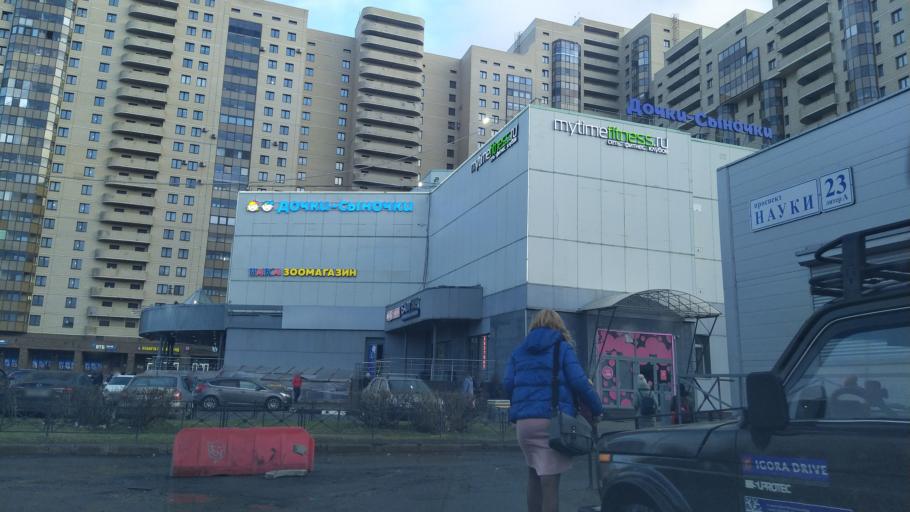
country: RU
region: Leningrad
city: Akademicheskoe
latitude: 60.0110
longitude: 30.4028
